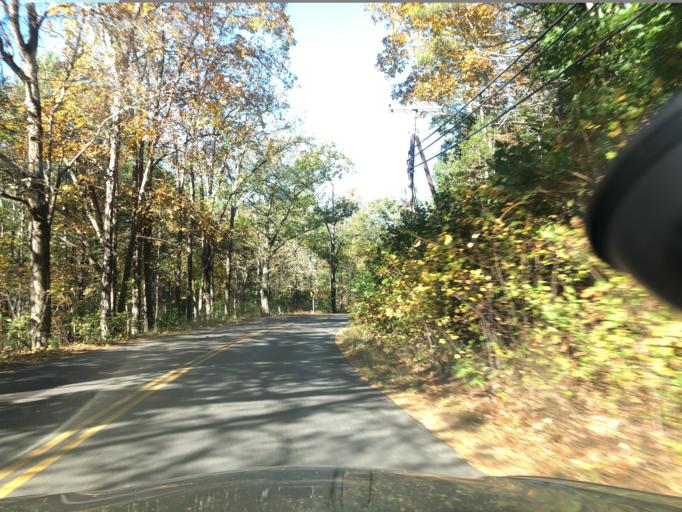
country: US
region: New Hampshire
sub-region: Rockingham County
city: Newmarket
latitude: 43.1042
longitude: -70.9537
